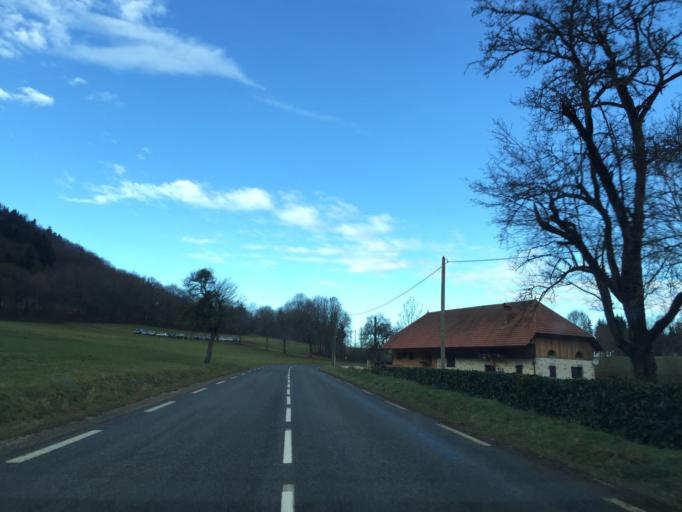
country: FR
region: Rhone-Alpes
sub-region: Departement de la Haute-Savoie
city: Gruffy
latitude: 45.7565
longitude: 6.0595
